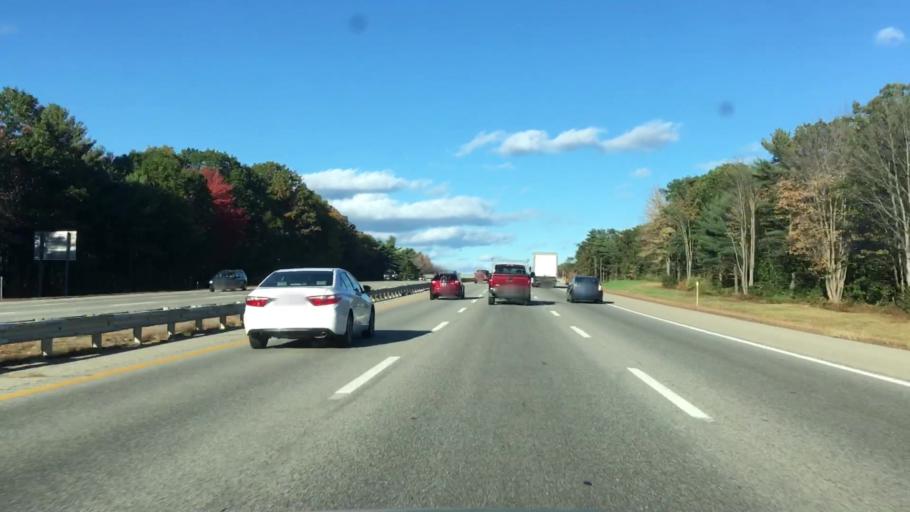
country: US
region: Maine
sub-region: Cumberland County
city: West Scarborough
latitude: 43.5511
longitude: -70.4278
